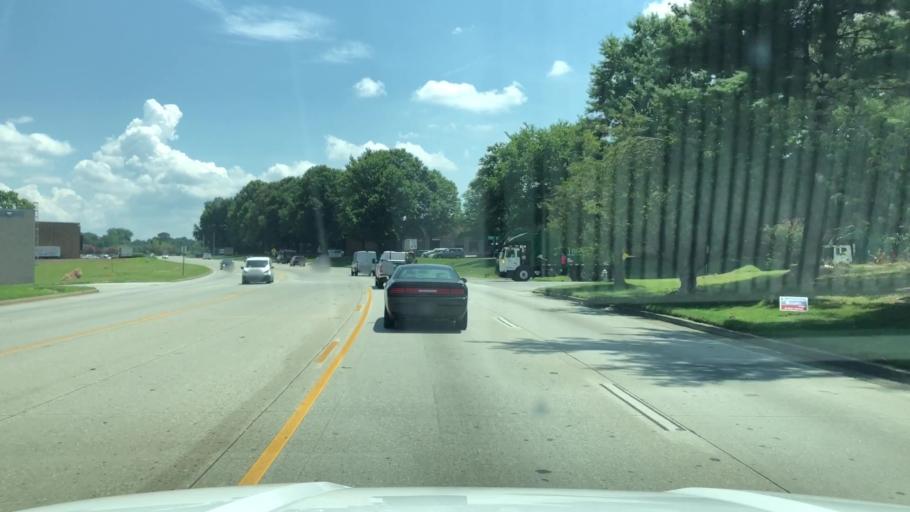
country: US
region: Georgia
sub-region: Gwinnett County
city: Norcross
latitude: 33.9353
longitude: -84.2315
